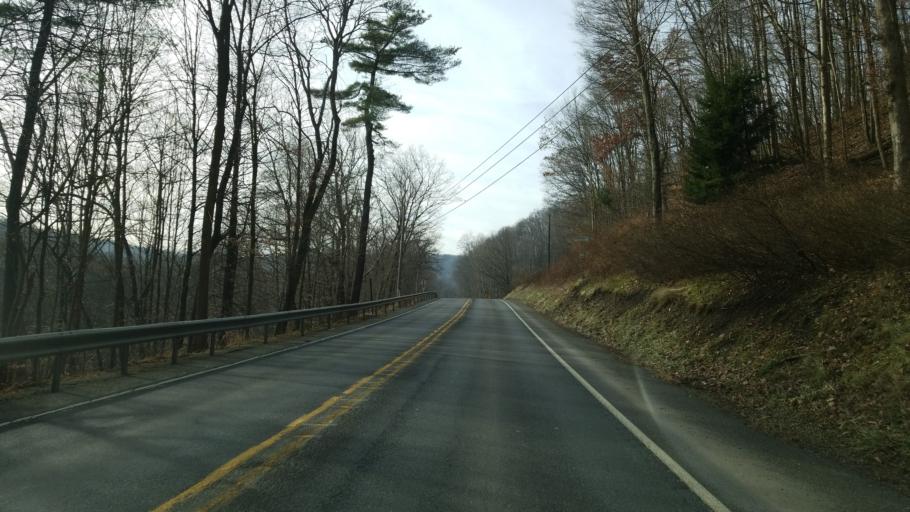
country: US
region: Pennsylvania
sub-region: Jefferson County
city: Albion
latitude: 40.9691
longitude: -78.8913
